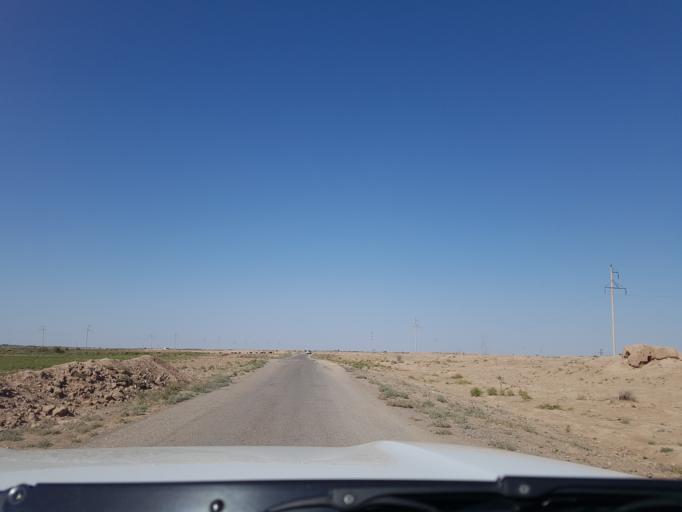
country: IR
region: Razavi Khorasan
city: Sarakhs
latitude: 36.5274
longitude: 61.2423
